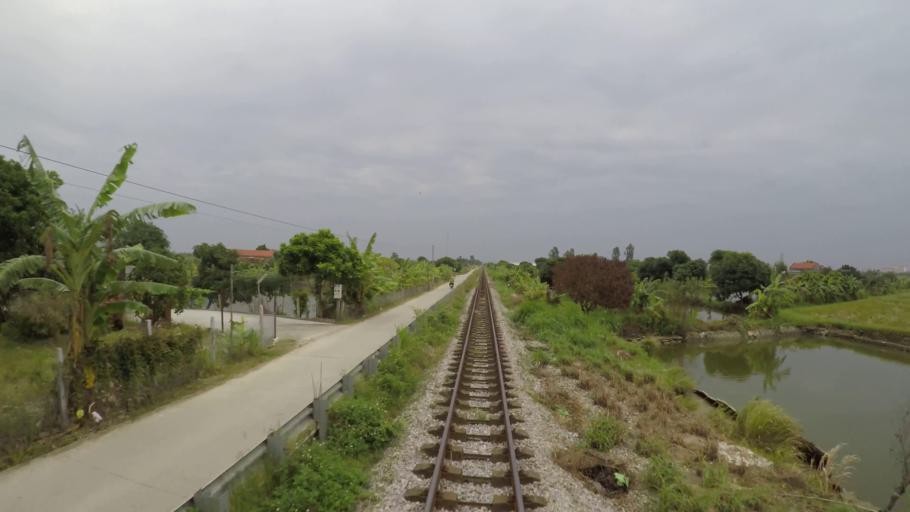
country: VN
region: Hai Duong
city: Lai Cach
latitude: 20.9534
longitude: 106.2260
